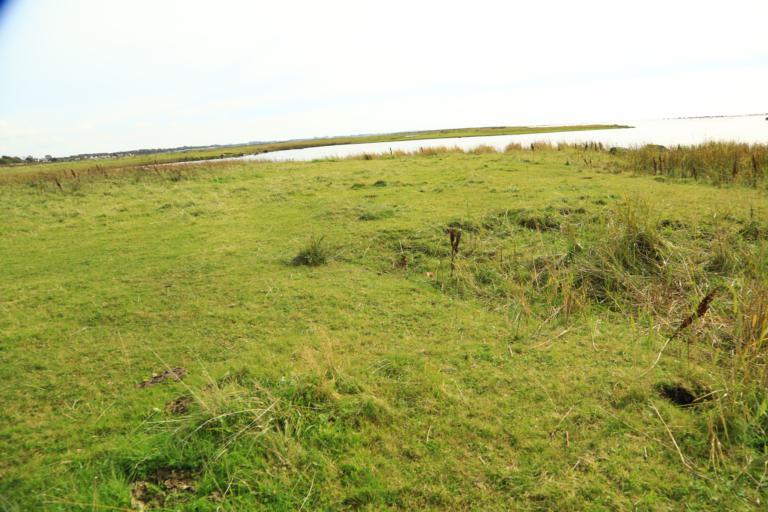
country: SE
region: Halland
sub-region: Varbergs Kommun
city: Traslovslage
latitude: 57.0208
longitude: 12.3342
